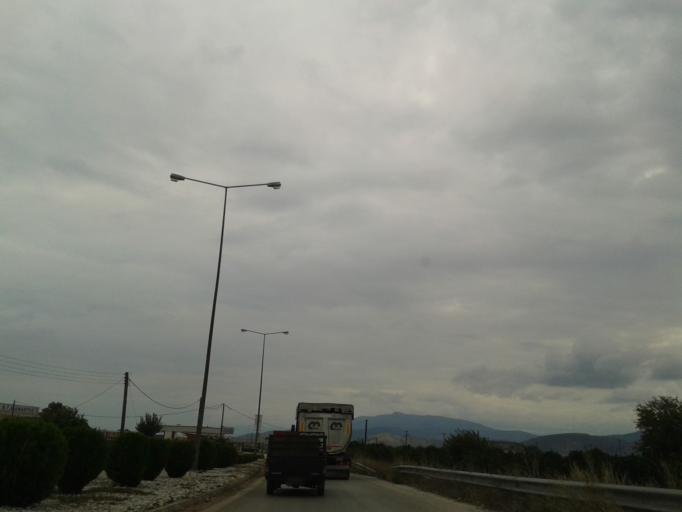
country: GR
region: Peloponnese
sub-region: Nomos Argolidos
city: Argos
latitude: 37.6145
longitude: 22.7114
